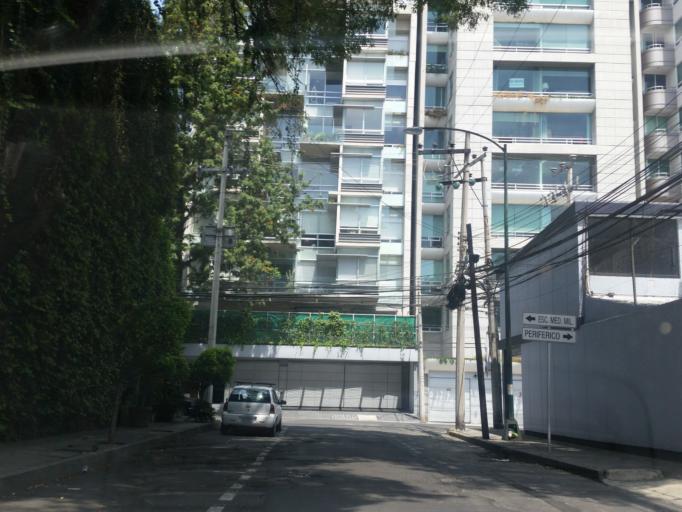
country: MX
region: Mexico City
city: Miguel Hidalgo
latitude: 19.4329
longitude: -99.2110
